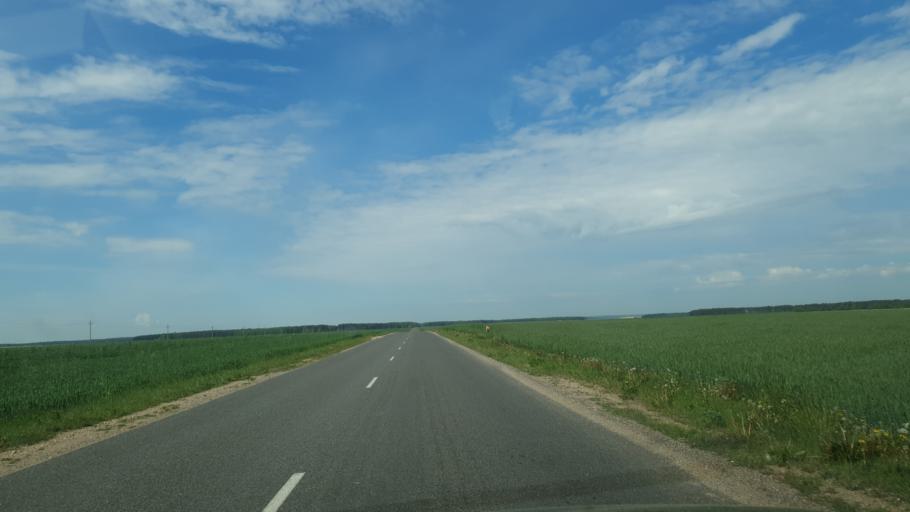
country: BY
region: Grodnenskaya
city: Mir
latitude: 53.4372
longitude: 26.4246
